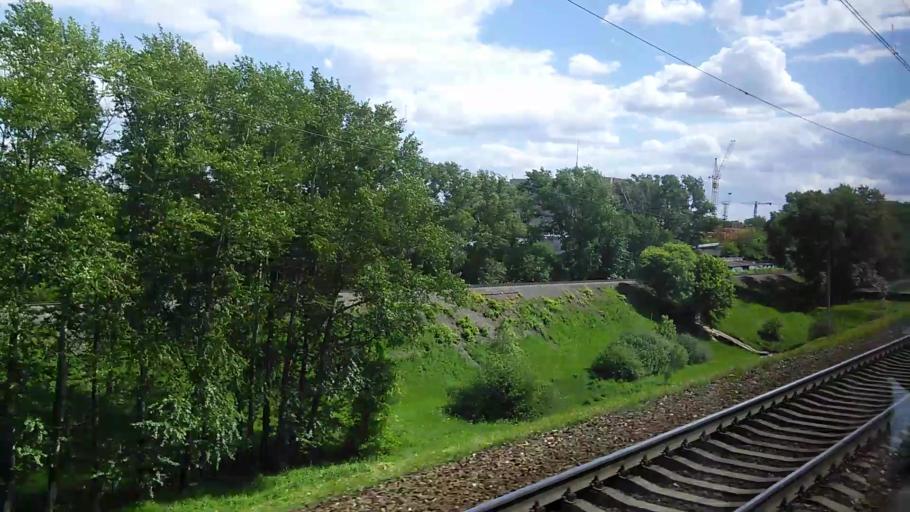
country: RU
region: Moscow
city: Likhobory
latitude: 55.8538
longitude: 37.5727
